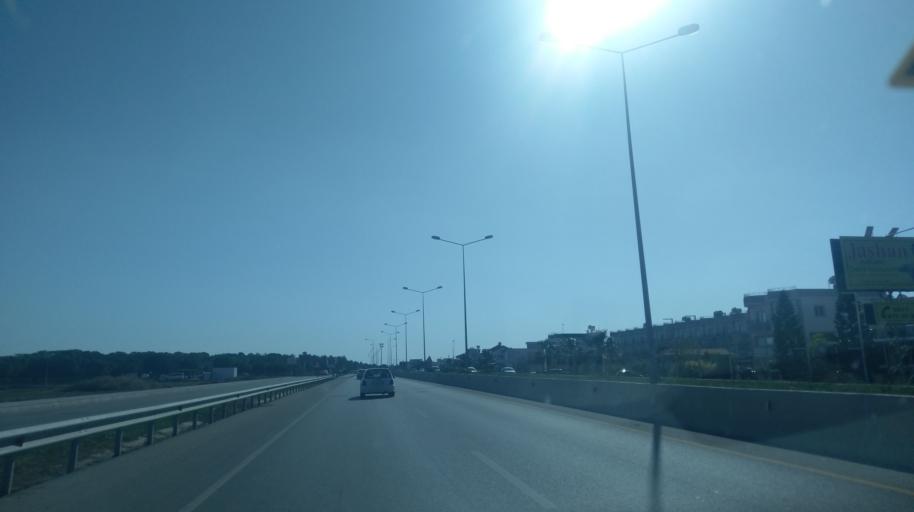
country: CY
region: Ammochostos
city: Trikomo
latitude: 35.2075
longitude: 33.8940
